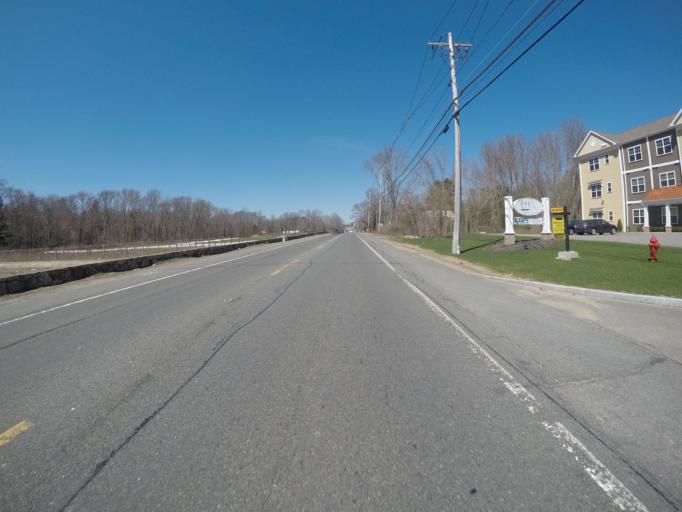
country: US
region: Massachusetts
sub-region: Norfolk County
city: Stoughton
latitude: 42.0705
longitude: -71.0874
